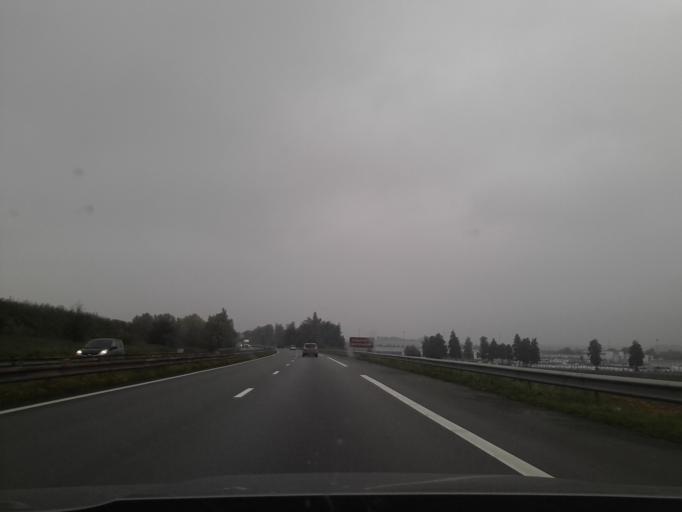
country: FR
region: Nord-Pas-de-Calais
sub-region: Departement du Nord
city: Lieu-Saint-Amand
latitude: 50.2761
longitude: 3.3383
